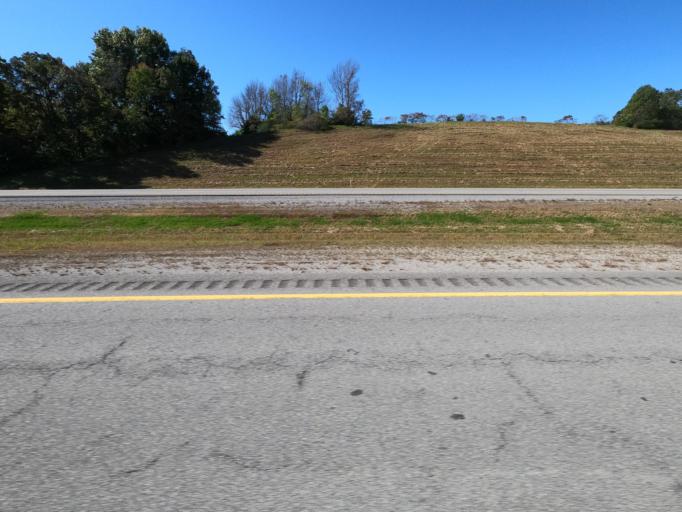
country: US
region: Tennessee
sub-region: Williamson County
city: Fairview
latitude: 35.9207
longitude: -87.1721
